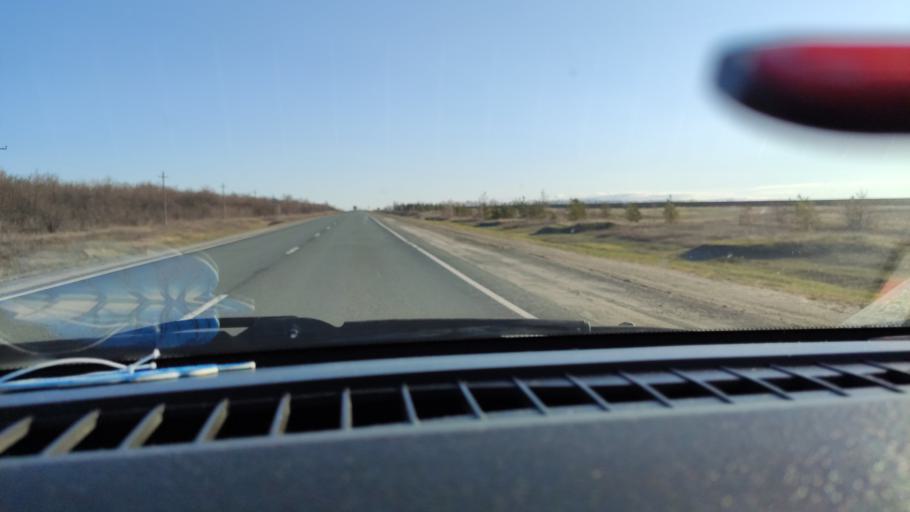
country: RU
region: Saratov
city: Alekseyevka
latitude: 52.2566
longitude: 47.9170
